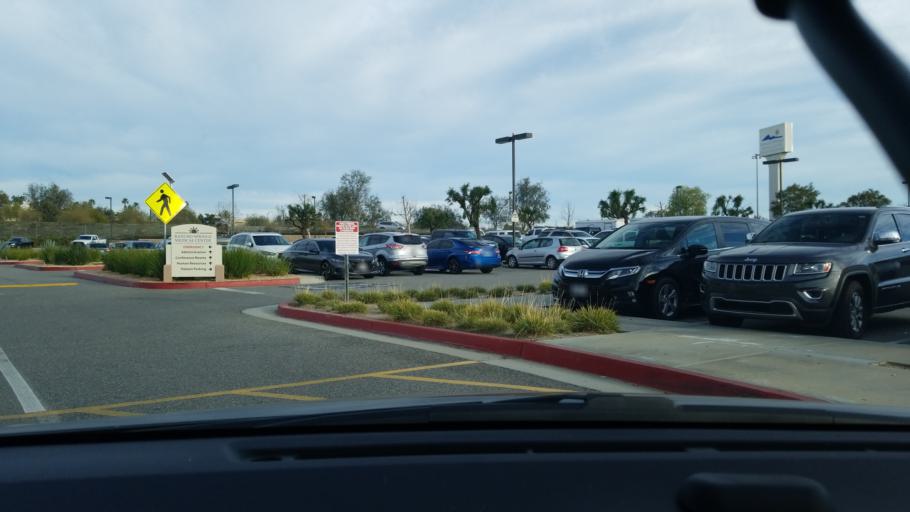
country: US
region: California
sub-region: Riverside County
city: Murrieta Hot Springs
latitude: 33.5580
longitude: -117.1831
